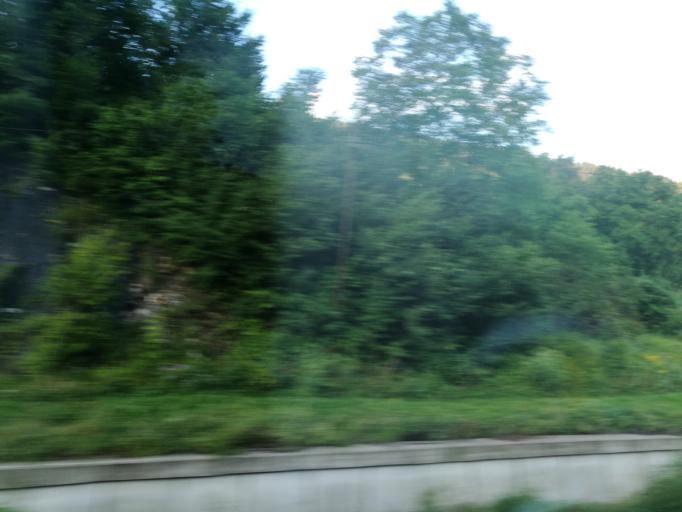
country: RO
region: Prahova
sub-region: Comuna Comarnic
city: Posada
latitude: 45.2864
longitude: 25.6131
